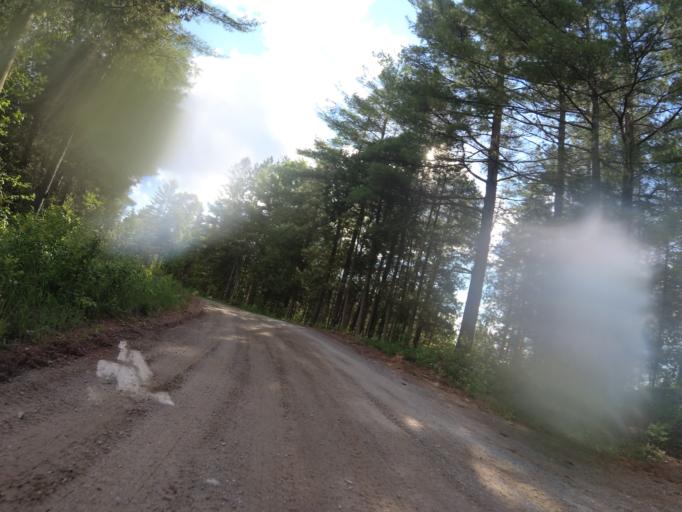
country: CA
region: Ontario
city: Renfrew
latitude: 45.1667
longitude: -76.9414
